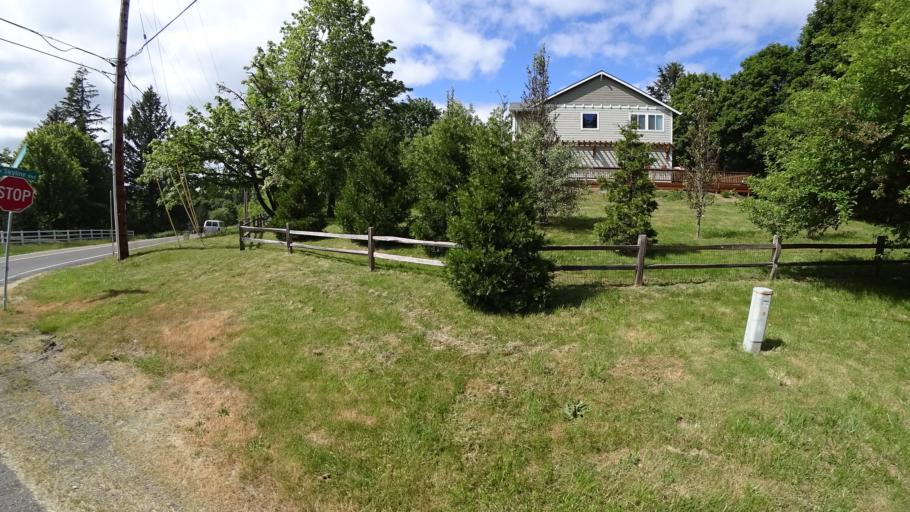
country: US
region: Oregon
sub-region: Washington County
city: Bethany
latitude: 45.6057
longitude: -122.8333
